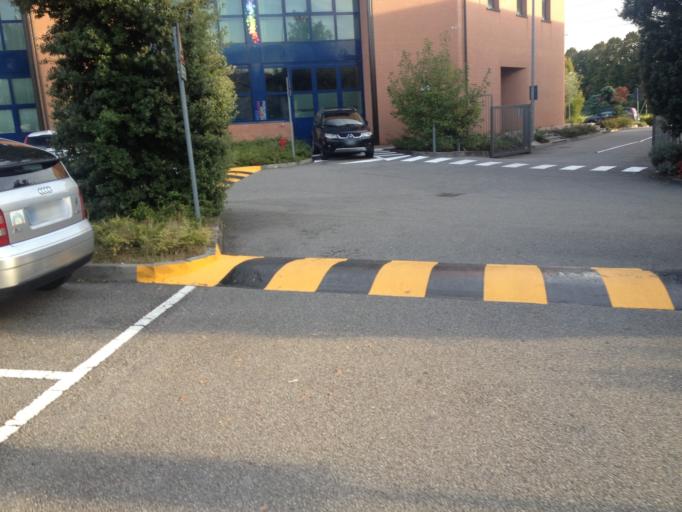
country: IT
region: Lombardy
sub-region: Provincia di Monza e Brianza
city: Velasca
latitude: 45.6333
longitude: 9.3554
